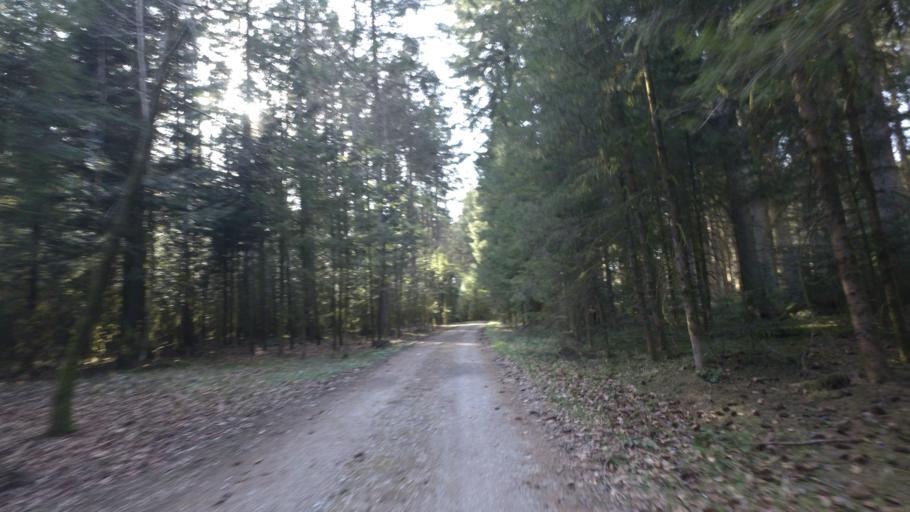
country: DE
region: Bavaria
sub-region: Upper Bavaria
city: Nussdorf
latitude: 47.9159
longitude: 12.5981
